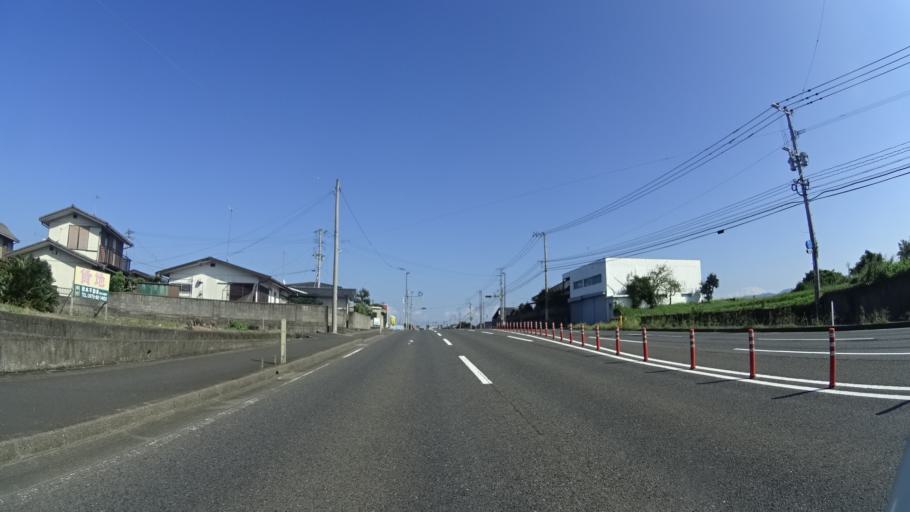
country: JP
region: Fukuoka
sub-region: Buzen-shi
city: Buzen
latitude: 33.6078
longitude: 131.1139
